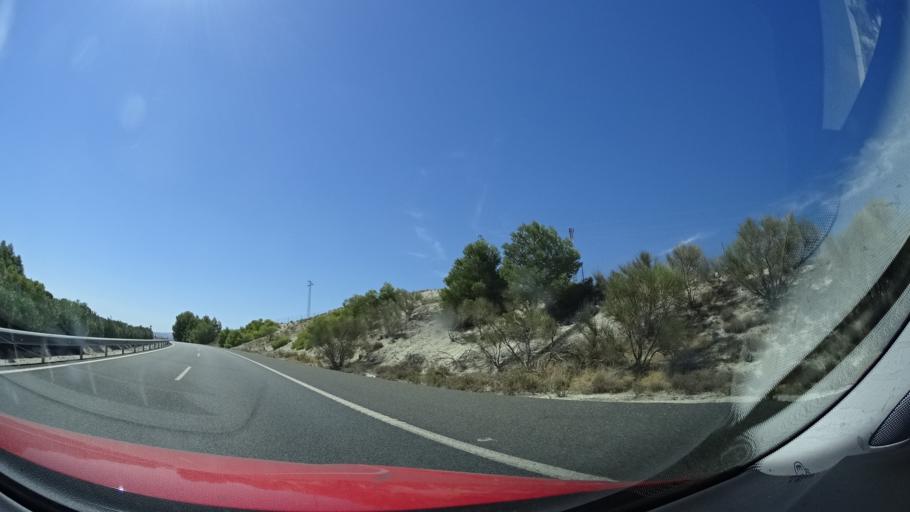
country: ES
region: Andalusia
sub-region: Provincia de Sevilla
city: Estepa
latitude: 37.2930
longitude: -4.9053
